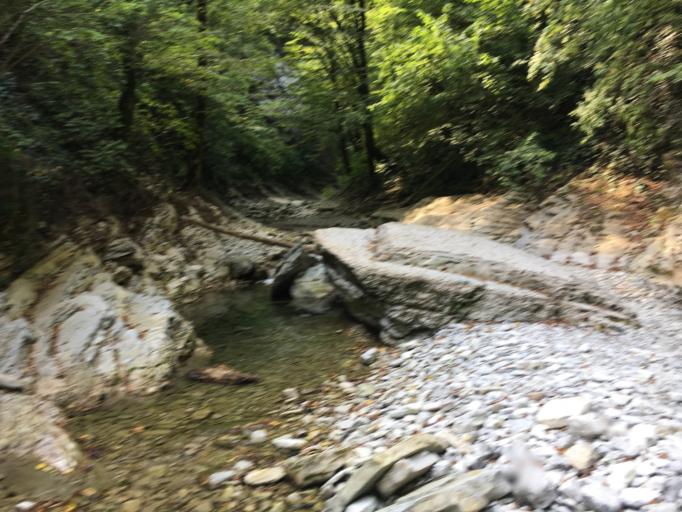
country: RU
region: Krasnodarskiy
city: Tuapse
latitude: 44.2630
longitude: 39.2022
